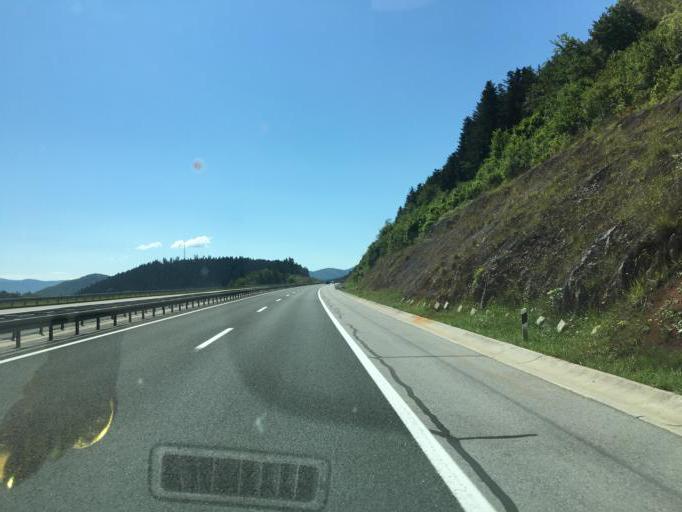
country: HR
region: Licko-Senjska
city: Otocac
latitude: 44.8554
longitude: 15.2228
